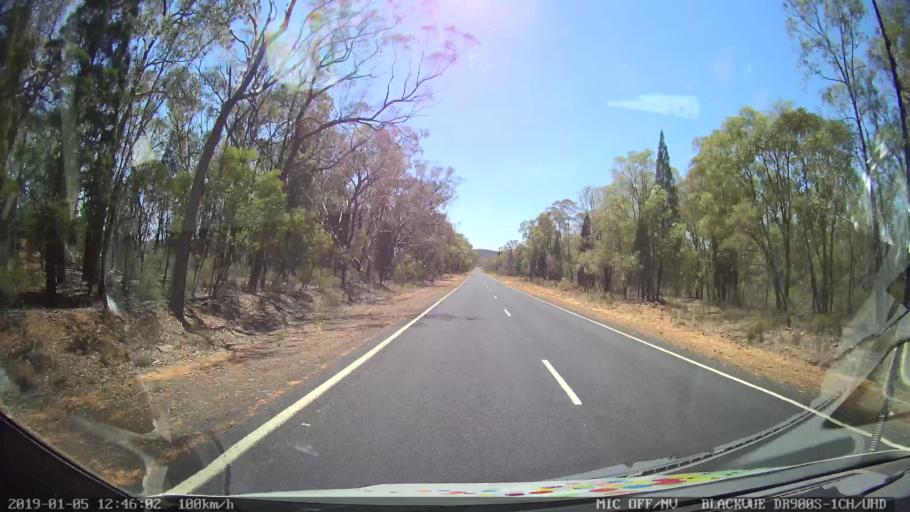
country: AU
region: New South Wales
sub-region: Warrumbungle Shire
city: Coonabarabran
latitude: -31.1221
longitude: 149.5573
